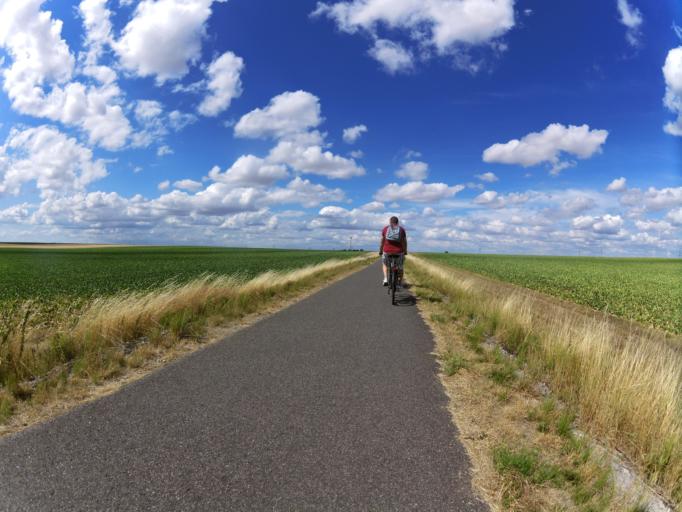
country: DE
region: Bavaria
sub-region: Regierungsbezirk Unterfranken
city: Sonderhofen
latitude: 49.5763
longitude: 10.0112
